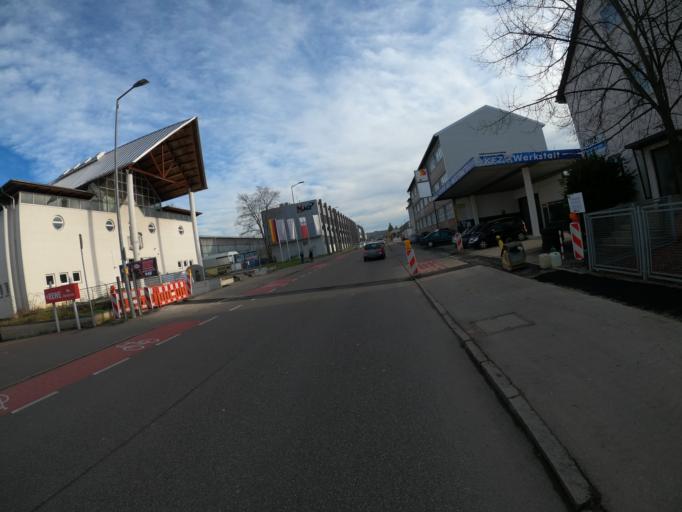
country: DE
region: Baden-Wuerttemberg
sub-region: Regierungsbezirk Stuttgart
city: Eislingen
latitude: 48.6964
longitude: 9.7174
